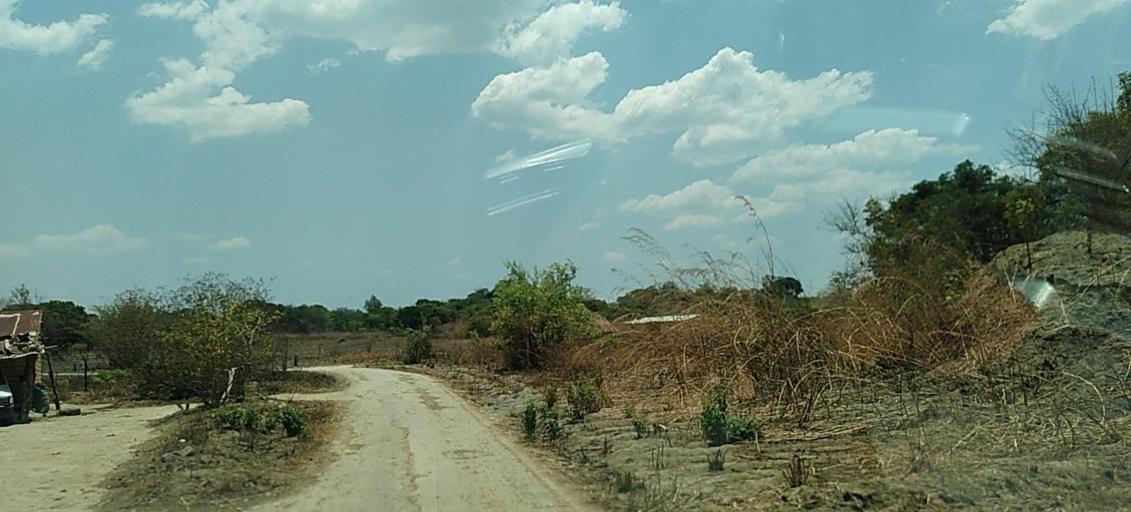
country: ZM
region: Copperbelt
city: Chililabombwe
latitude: -12.4846
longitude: 27.6696
